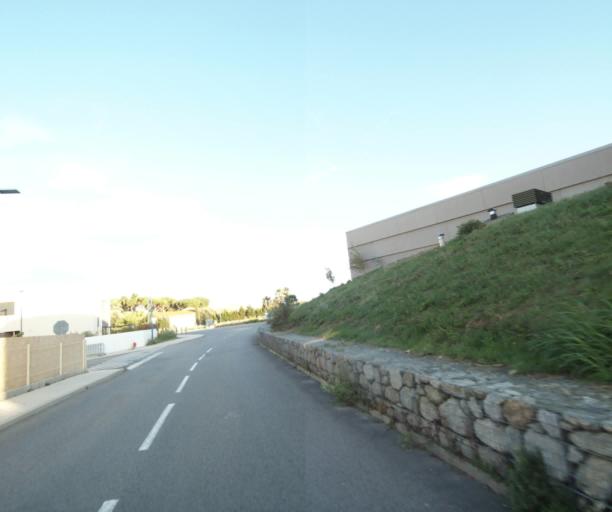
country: FR
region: Languedoc-Roussillon
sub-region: Departement des Pyrenees-Orientales
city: Argelers
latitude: 42.5676
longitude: 3.0048
